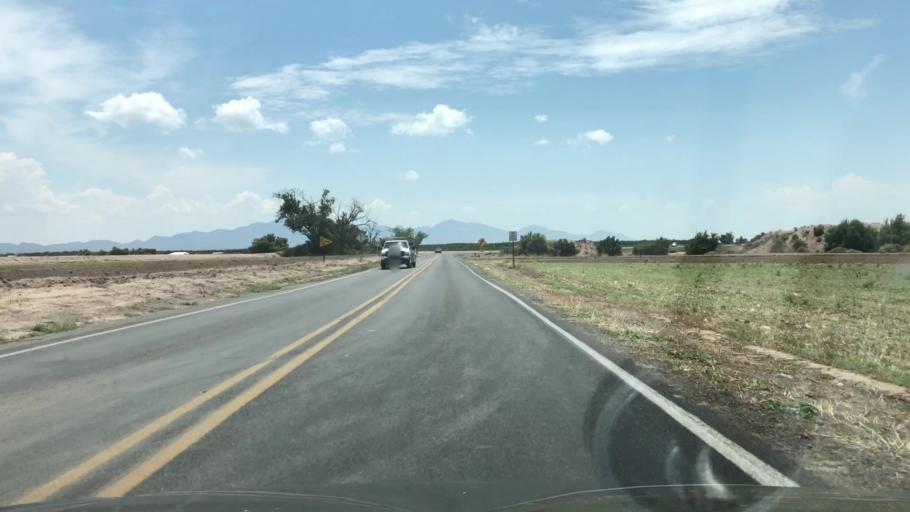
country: US
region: New Mexico
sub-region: Dona Ana County
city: Vado
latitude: 32.0702
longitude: -106.6822
